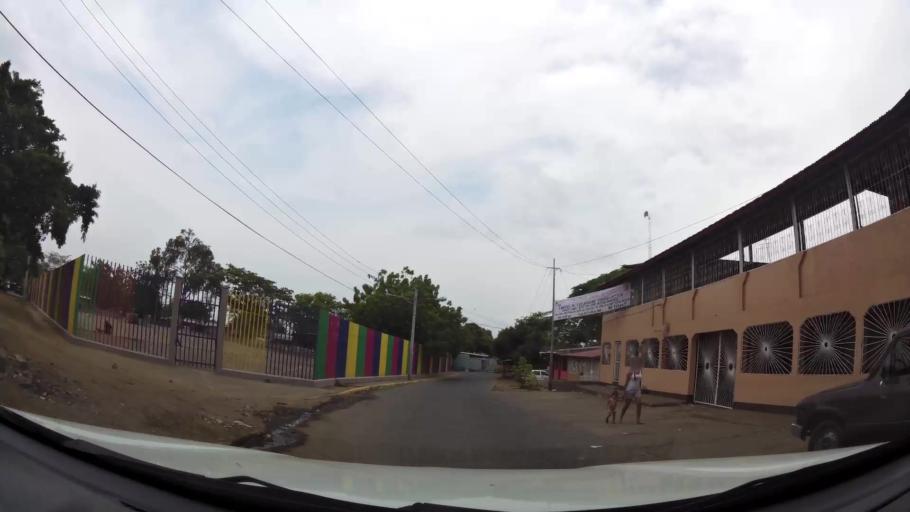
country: NI
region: Managua
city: Managua
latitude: 12.1245
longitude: -86.2378
